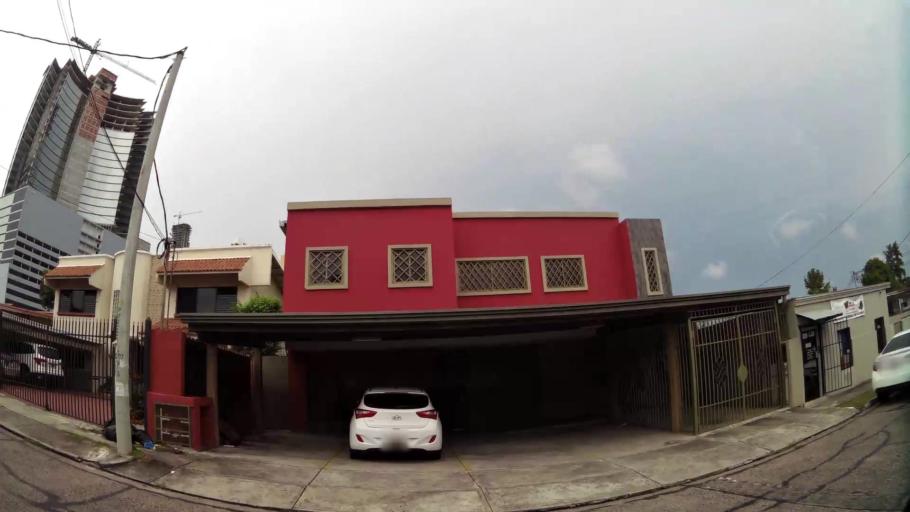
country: PA
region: Panama
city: Panama
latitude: 9.0005
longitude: -79.5311
